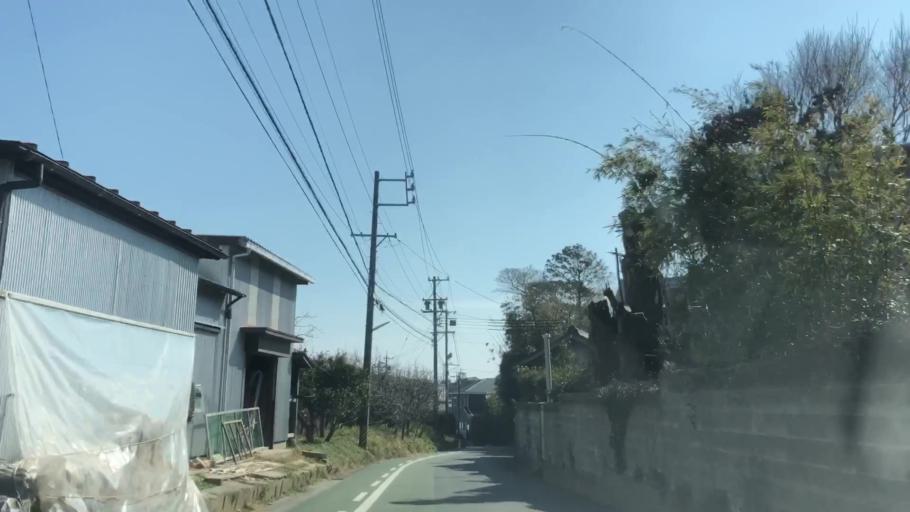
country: JP
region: Aichi
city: Tahara
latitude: 34.6659
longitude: 137.2570
